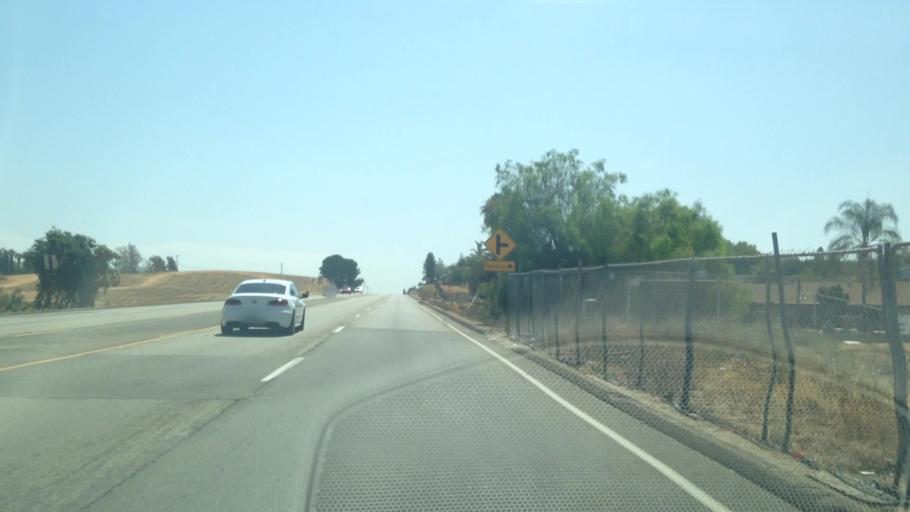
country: US
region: California
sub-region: Riverside County
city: Woodcrest
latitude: 33.8823
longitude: -117.3795
